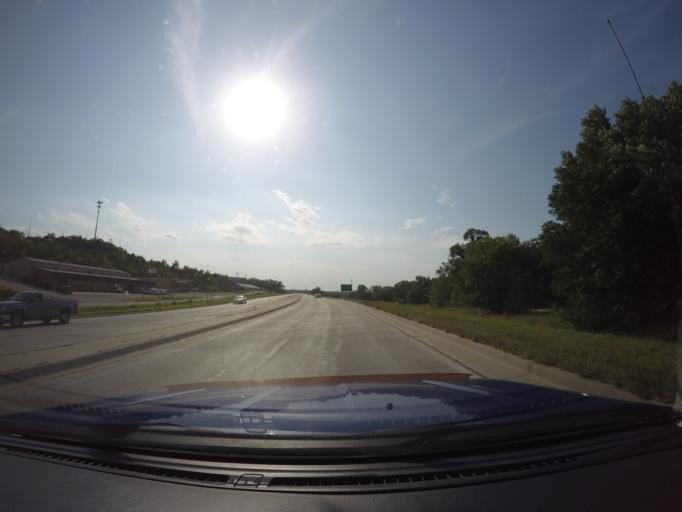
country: US
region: Kansas
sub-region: Riley County
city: Manhattan
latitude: 39.1735
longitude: -96.5486
